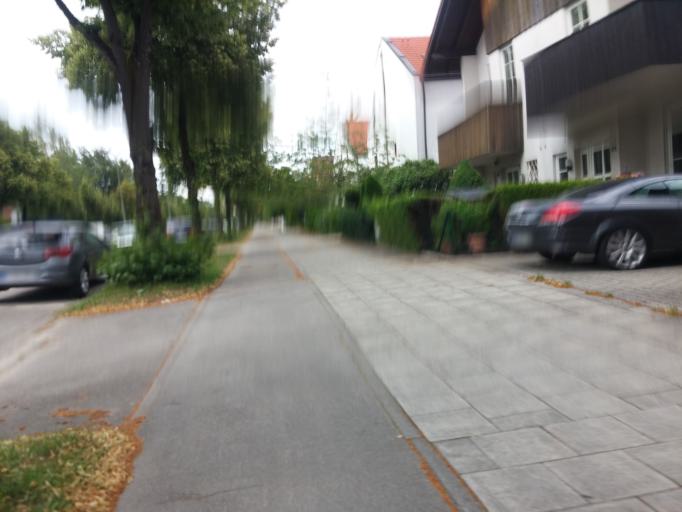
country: DE
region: Bavaria
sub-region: Upper Bavaria
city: Bogenhausen
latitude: 48.1610
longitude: 11.6223
